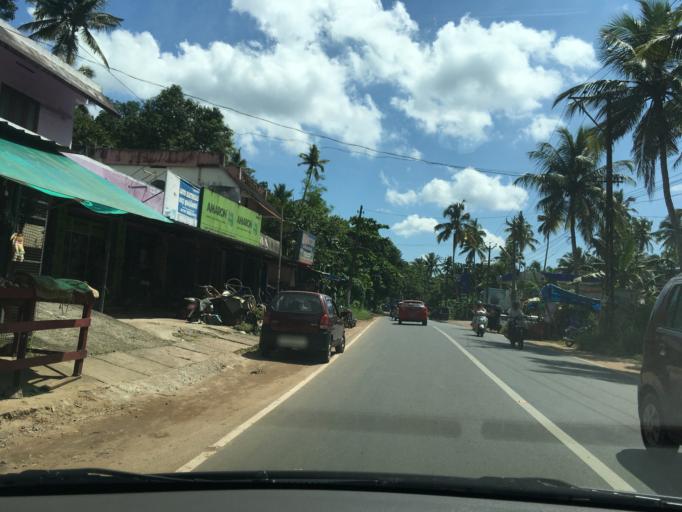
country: IN
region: Kerala
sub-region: Thiruvananthapuram
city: Nedumangad
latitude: 8.5930
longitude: 76.9951
